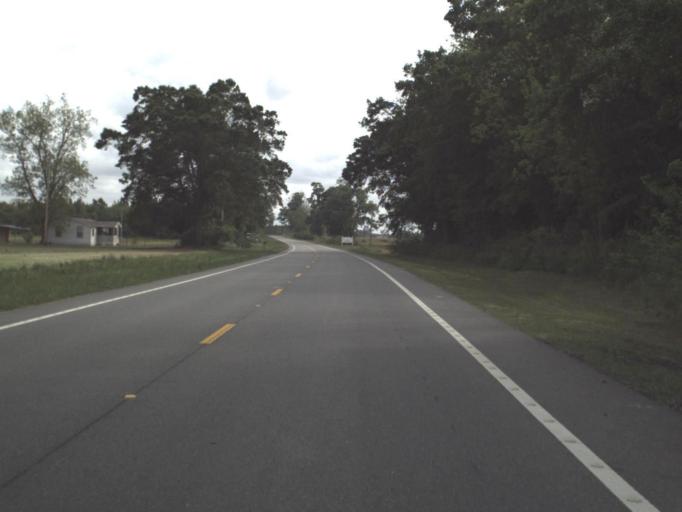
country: US
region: Alabama
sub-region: Escambia County
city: East Brewton
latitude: 30.9818
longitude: -87.0435
